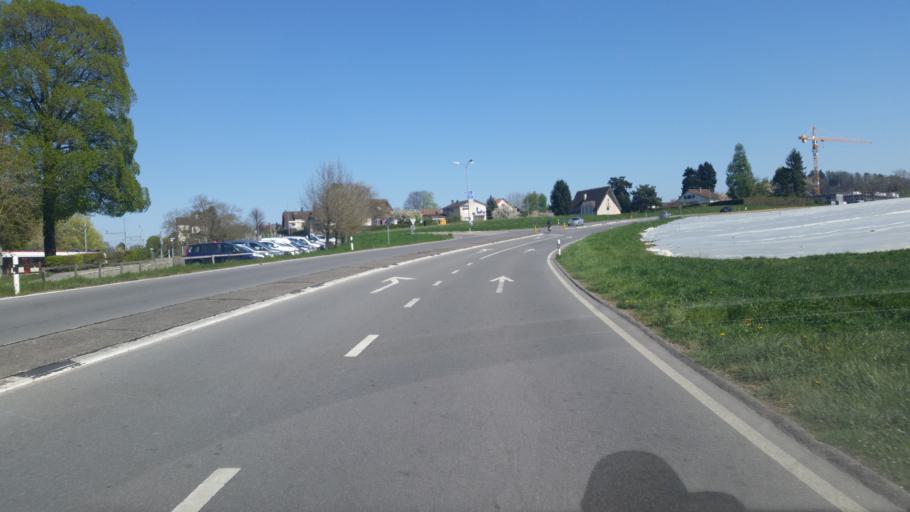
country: CH
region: Fribourg
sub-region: See District
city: Murten
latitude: 46.9260
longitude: 7.1235
